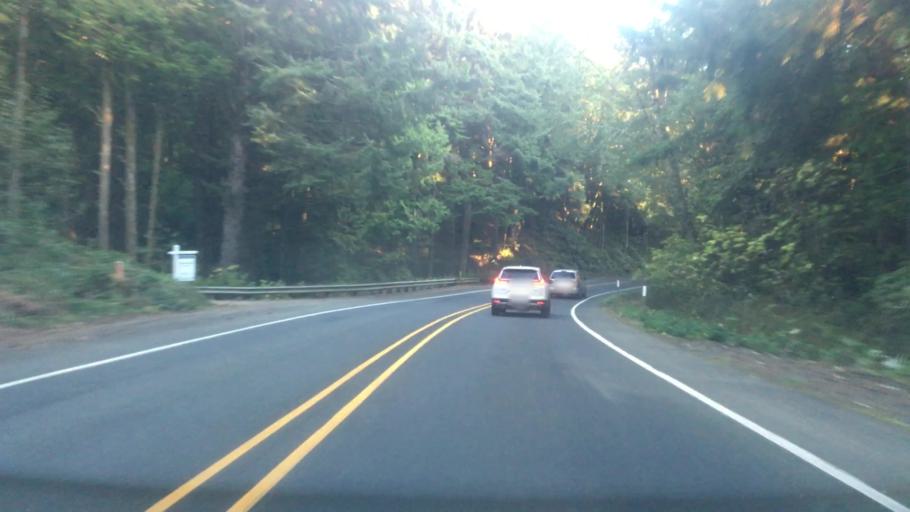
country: US
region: Oregon
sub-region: Clatsop County
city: Cannon Beach
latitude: 45.8415
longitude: -123.9584
